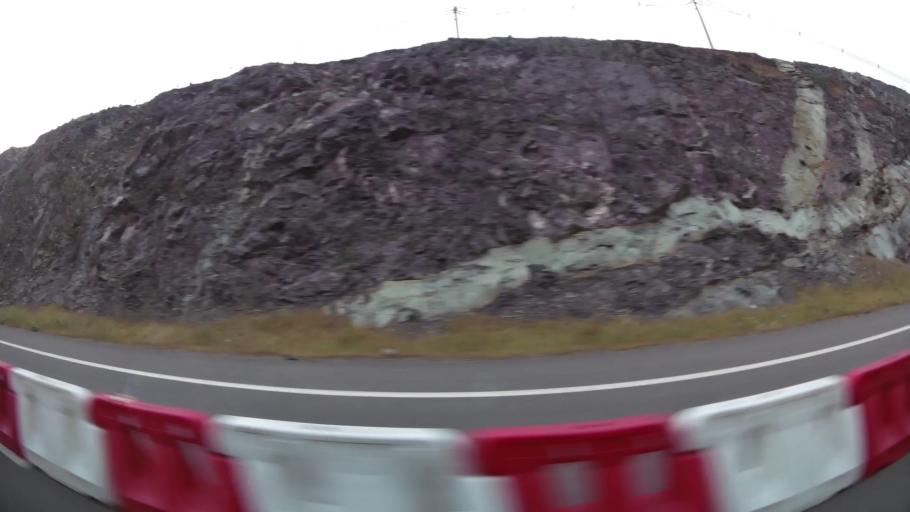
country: CL
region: Santiago Metropolitan
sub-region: Provincia de Chacabuco
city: Chicureo Abajo
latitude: -33.3289
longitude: -70.6272
